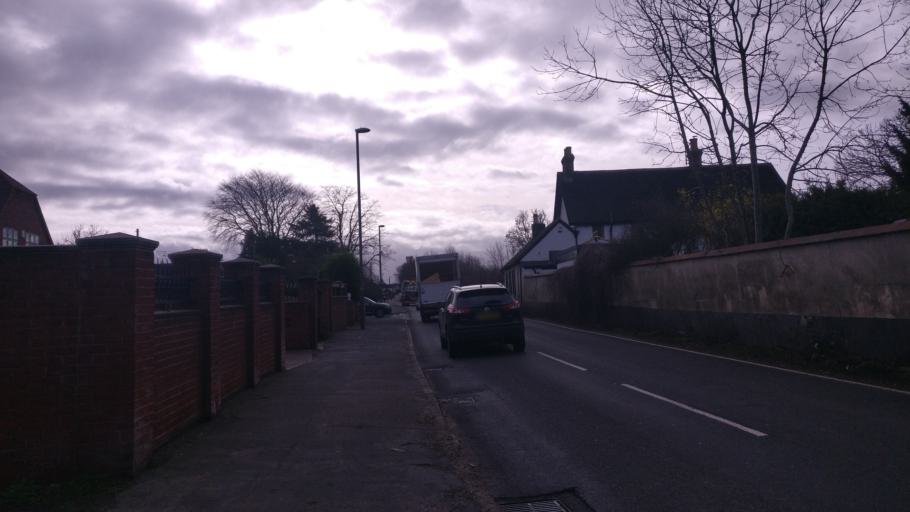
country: GB
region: England
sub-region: Surrey
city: Egham
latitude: 51.4210
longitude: -0.5359
